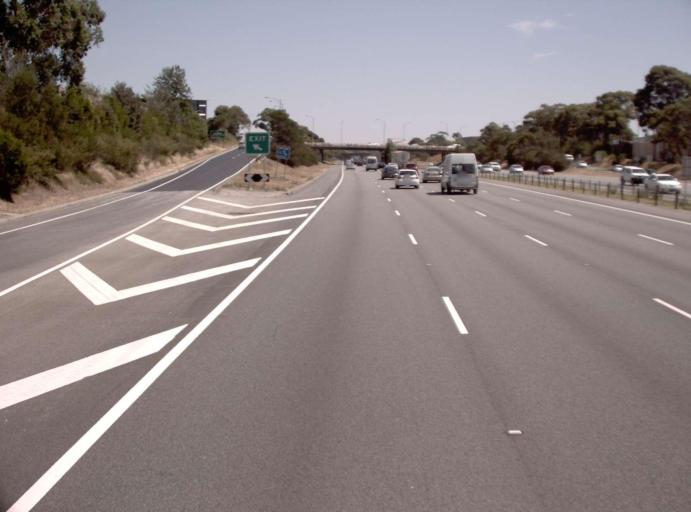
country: AU
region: Victoria
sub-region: Monash
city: Notting Hill
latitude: -37.9110
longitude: 145.1635
